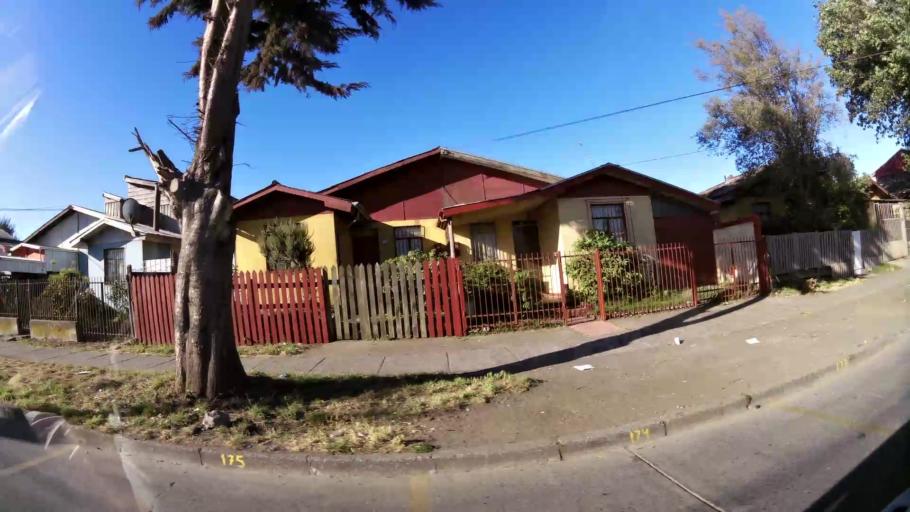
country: CL
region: Biobio
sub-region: Provincia de Concepcion
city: Concepcion
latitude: -36.8275
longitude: -73.1277
